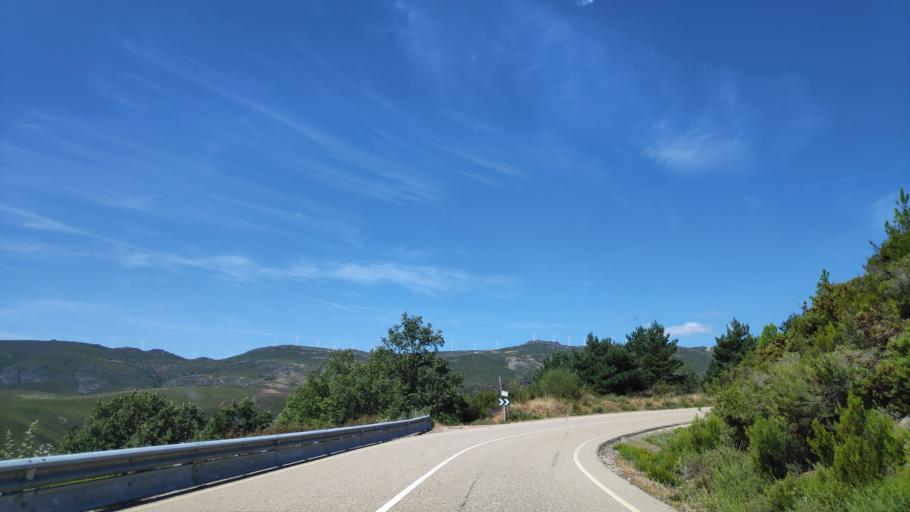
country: ES
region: Castille and Leon
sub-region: Provincia de Zamora
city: Requejo
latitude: 41.9816
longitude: -6.7114
